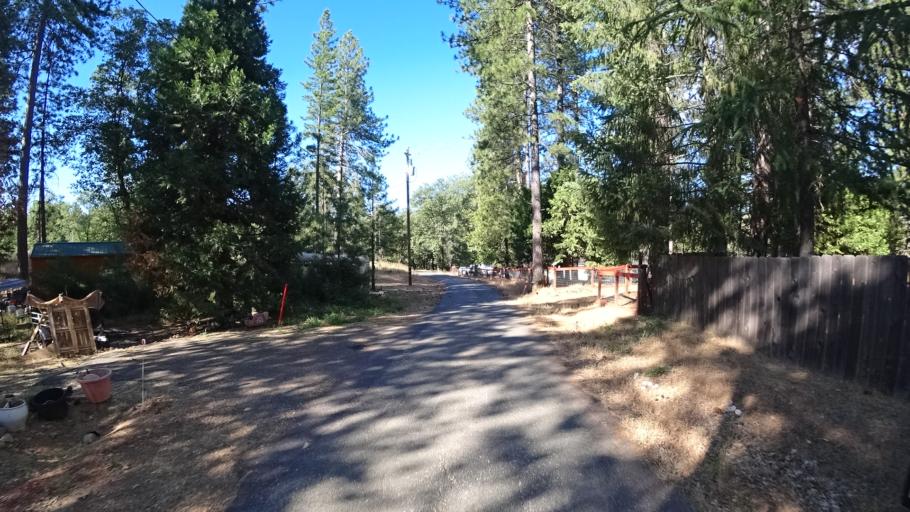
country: US
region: California
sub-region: Amador County
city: Pioneer
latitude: 38.3810
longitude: -120.5569
